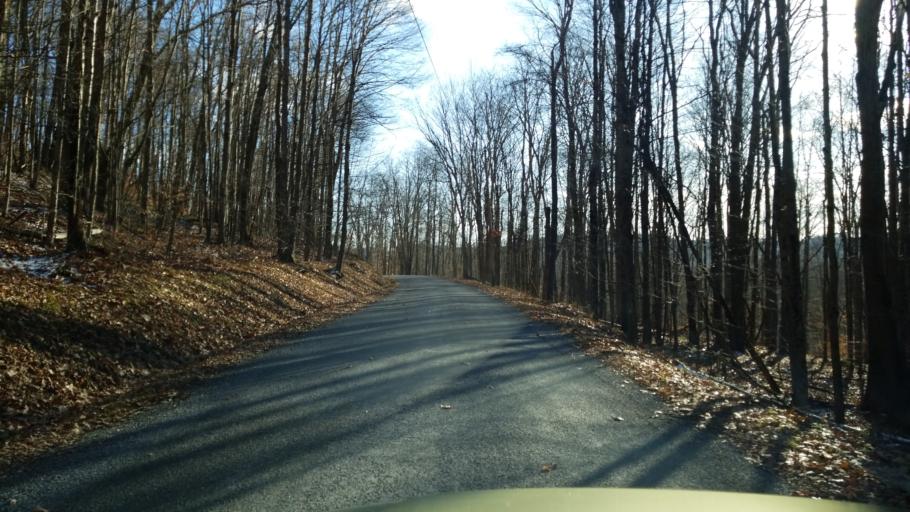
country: US
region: Pennsylvania
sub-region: Jefferson County
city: Brockway
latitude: 41.2708
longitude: -78.8057
